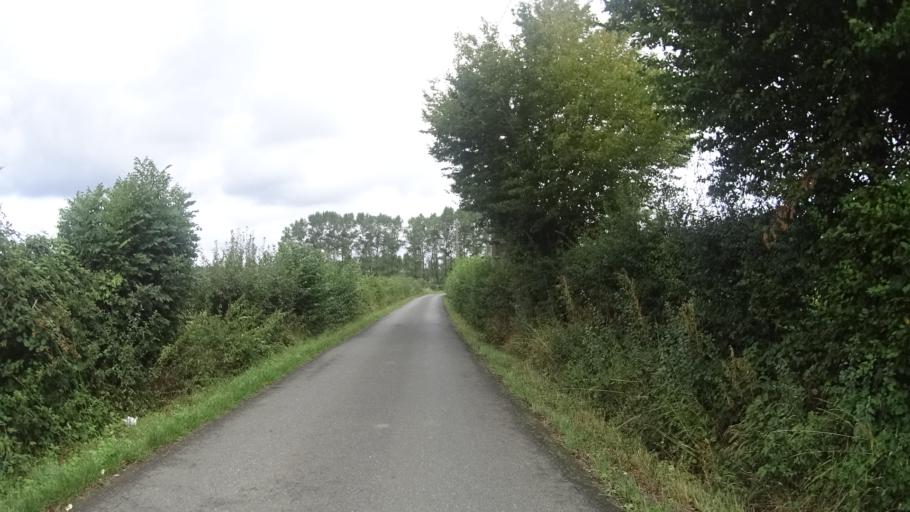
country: FR
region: Nord-Pas-de-Calais
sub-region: Departement du Nord
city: Maroilles
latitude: 50.1349
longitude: 3.7272
